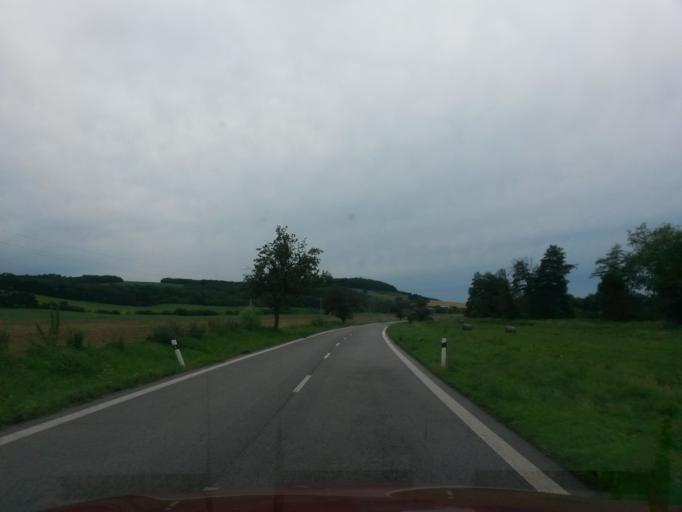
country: SK
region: Nitriansky
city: Sahy
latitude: 48.1591
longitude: 19.0009
